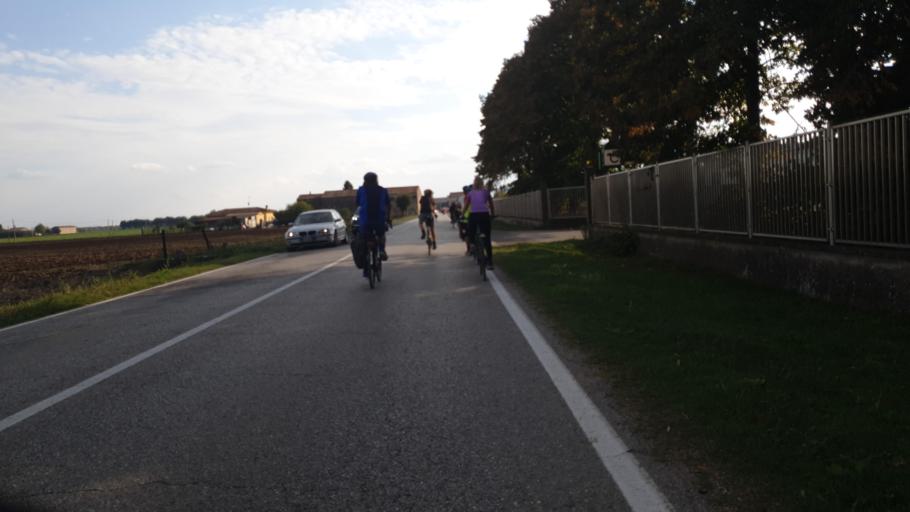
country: IT
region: Veneto
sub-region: Provincia di Vicenza
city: Poiana Maggiore
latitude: 45.2730
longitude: 11.4888
